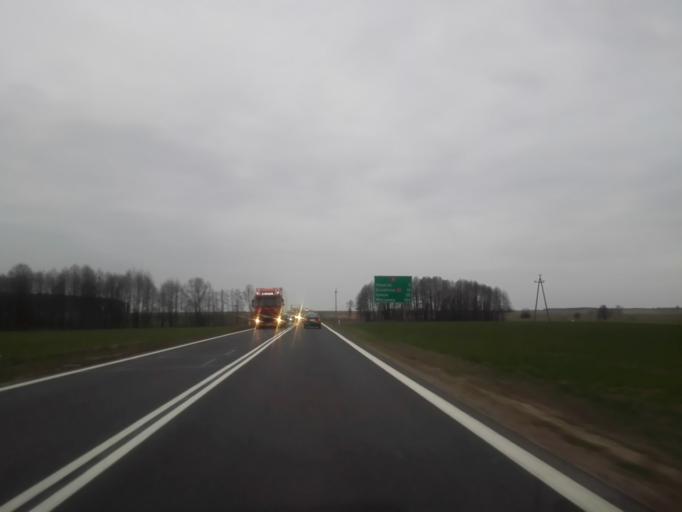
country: PL
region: Podlasie
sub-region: Powiat kolnenski
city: Stawiski
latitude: 53.4186
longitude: 22.1654
